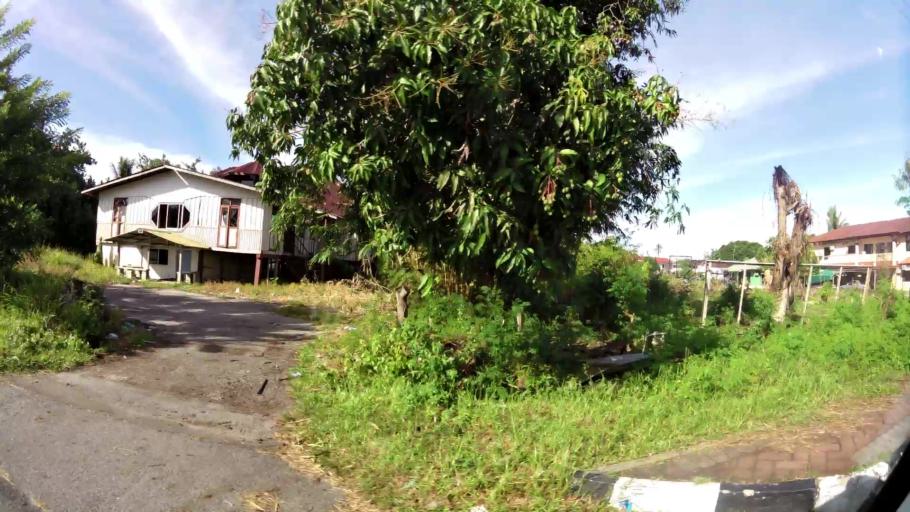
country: BN
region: Belait
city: Kuala Belait
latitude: 4.5846
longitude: 114.1876
